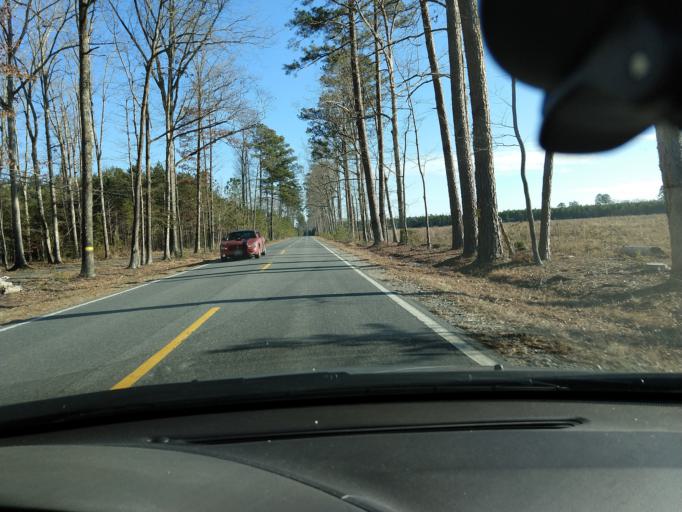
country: US
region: Virginia
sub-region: Charles City County
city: Charles City
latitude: 37.2868
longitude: -76.9259
